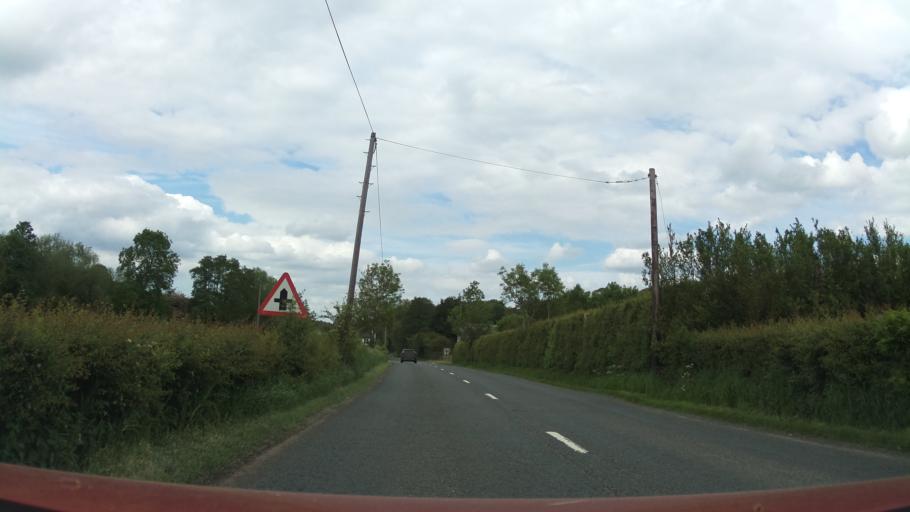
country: GB
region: England
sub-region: Herefordshire
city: Yatton
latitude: 51.9753
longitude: -2.5158
